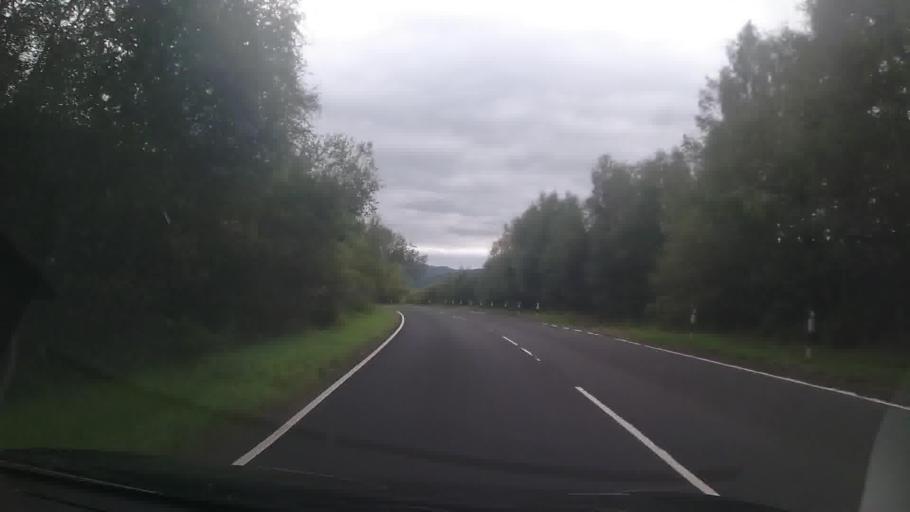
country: GB
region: Scotland
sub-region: Argyll and Bute
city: Garelochhead
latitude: 56.2292
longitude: -4.9969
